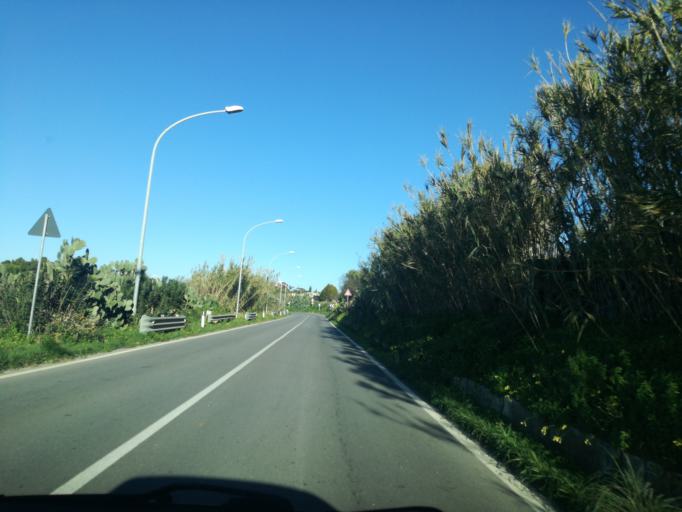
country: IT
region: Sicily
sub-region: Provincia di Caltanissetta
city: Gela
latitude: 37.1051
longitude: 14.1598
